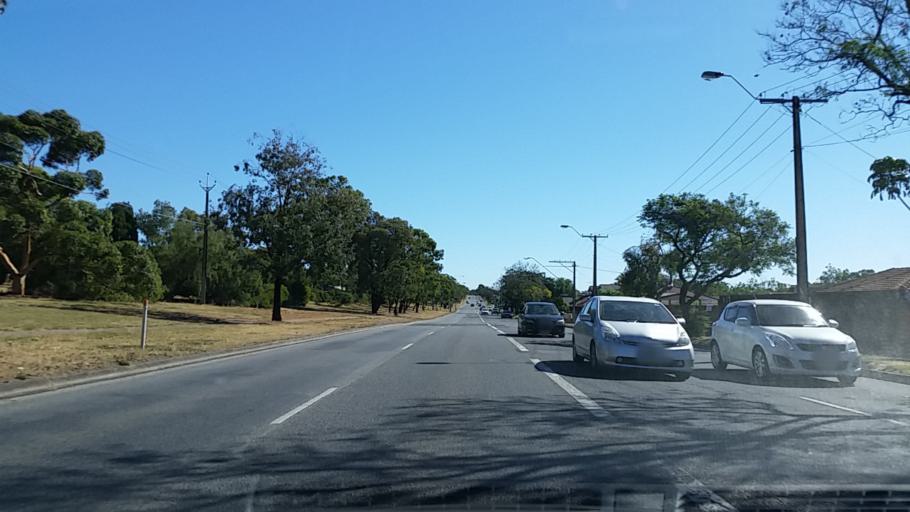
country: AU
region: South Australia
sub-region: Salisbury
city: Ingle Farm
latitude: -34.8257
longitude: 138.6344
